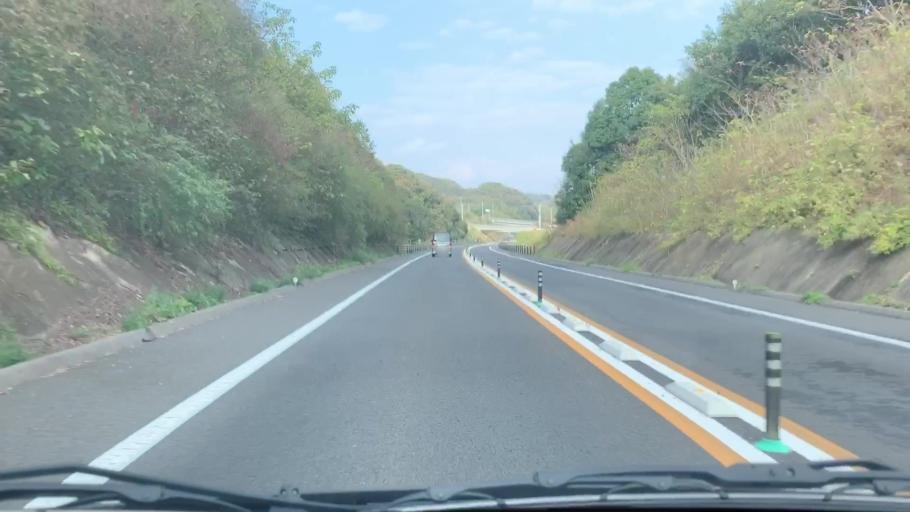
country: JP
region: Nagasaki
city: Sasebo
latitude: 33.0169
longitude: 129.7314
